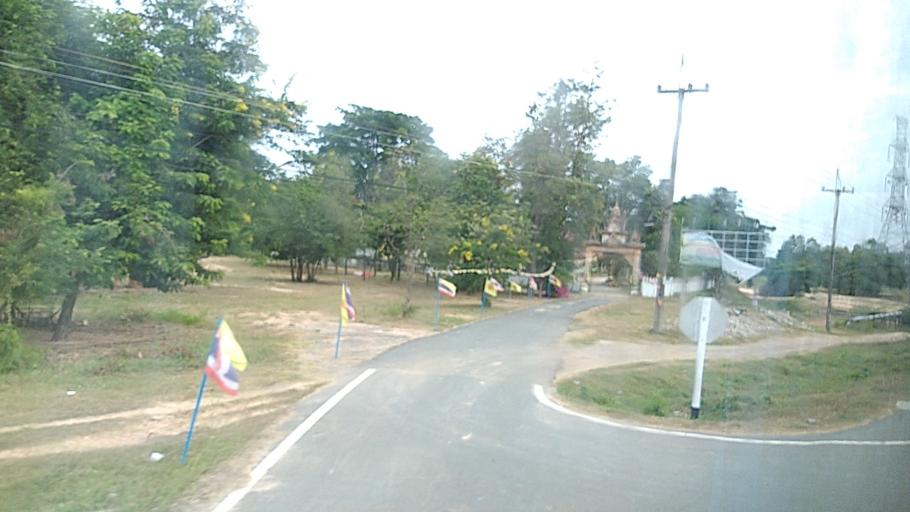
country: TH
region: Kalasin
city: Khong Chai
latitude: 16.1307
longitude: 103.4640
